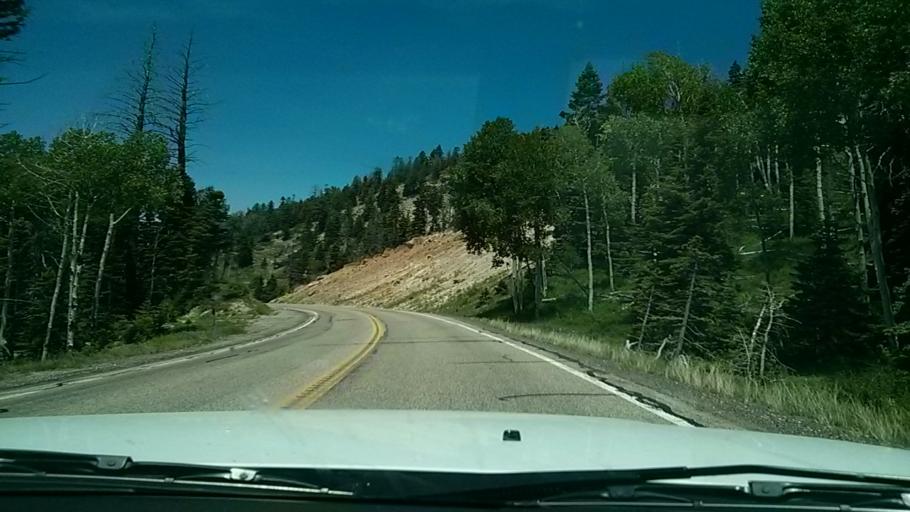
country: US
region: Utah
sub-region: Iron County
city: Cedar City
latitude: 37.5911
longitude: -112.8818
